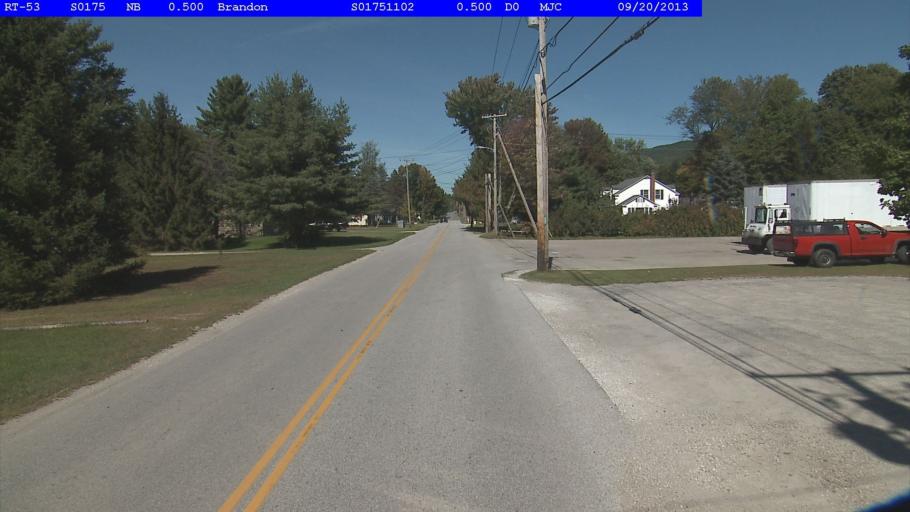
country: US
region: Vermont
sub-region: Rutland County
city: Brandon
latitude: 43.8339
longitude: -73.0555
